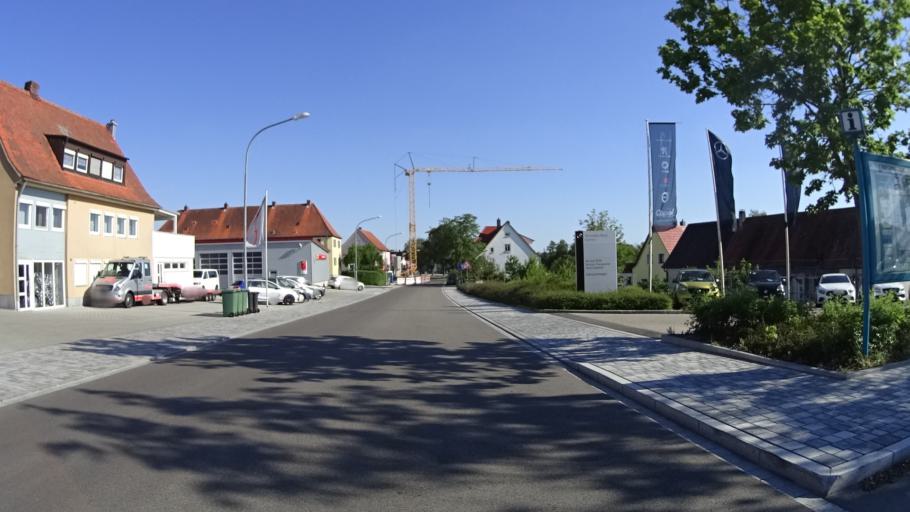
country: DE
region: Bavaria
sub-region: Regierungsbezirk Mittelfranken
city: Feuchtwangen
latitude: 49.1746
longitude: 10.3253
